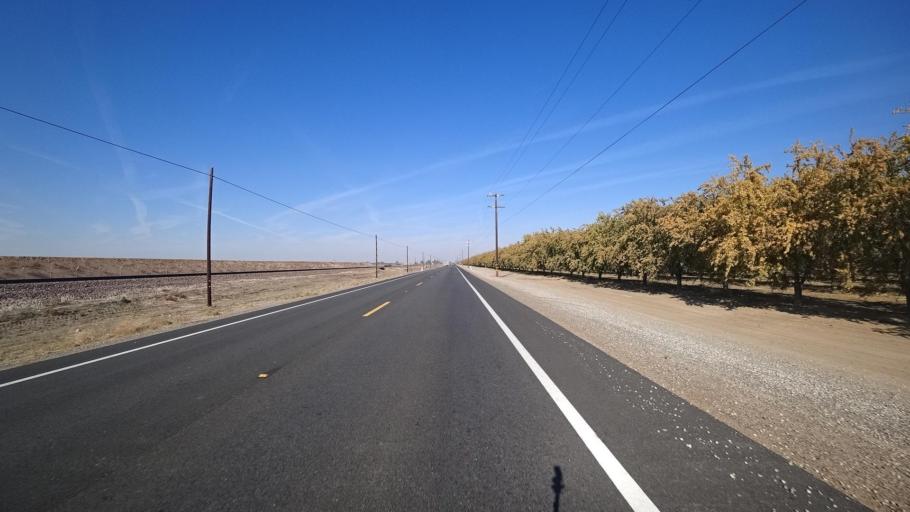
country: US
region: California
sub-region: Kern County
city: Wasco
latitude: 35.6471
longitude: -119.3310
